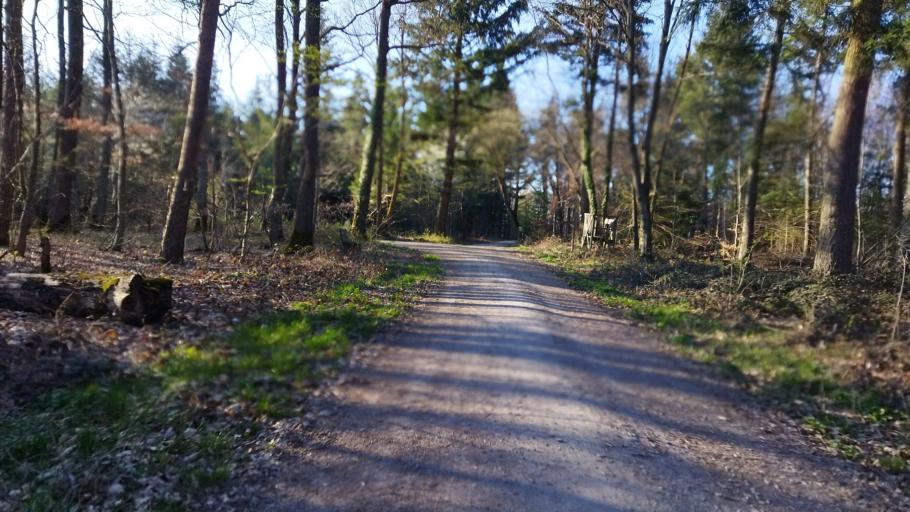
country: DE
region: Baden-Wuerttemberg
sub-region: Karlsruhe Region
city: Sternenfels
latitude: 49.0480
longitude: 8.8766
